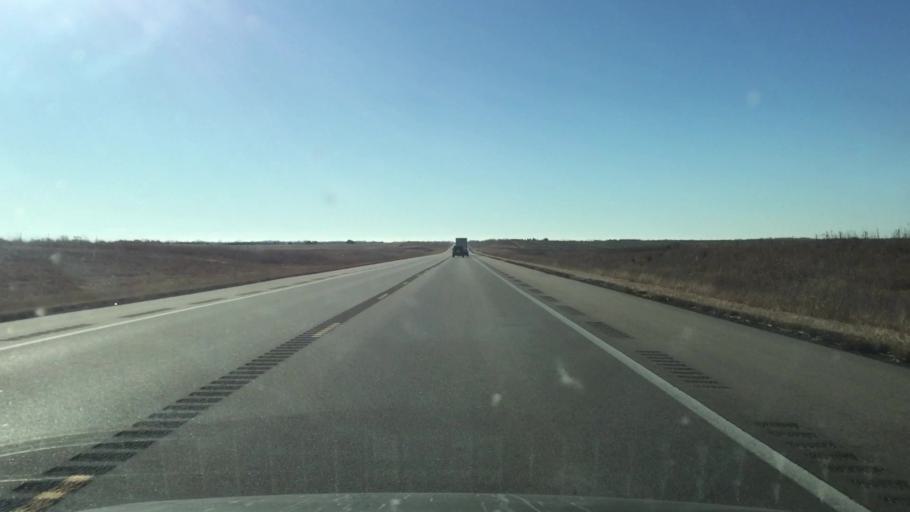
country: US
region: Kansas
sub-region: Allen County
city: Iola
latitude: 38.0584
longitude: -95.3805
